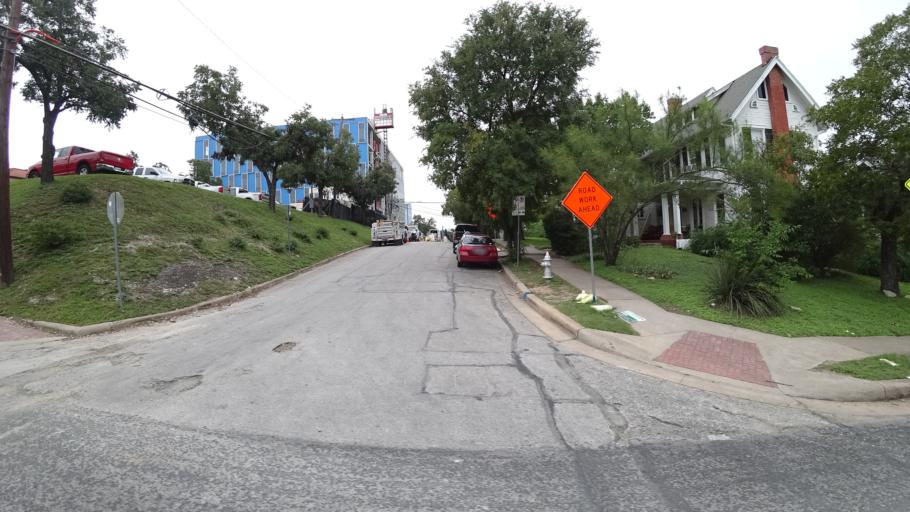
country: US
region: Texas
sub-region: Travis County
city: Austin
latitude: 30.2751
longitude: -97.7453
